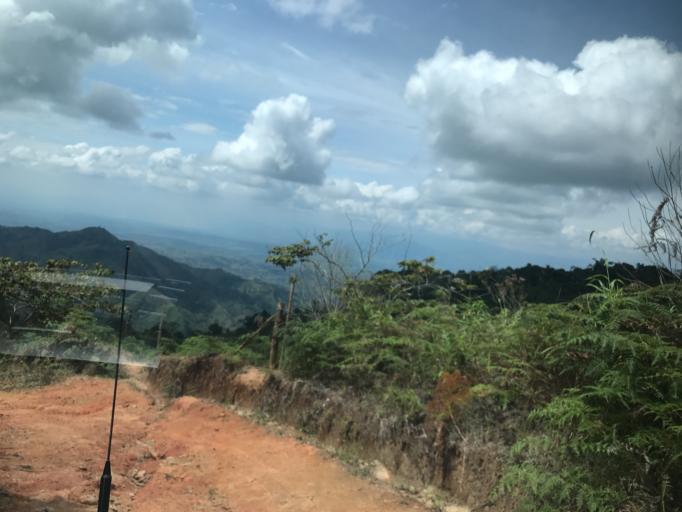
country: CO
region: Valle del Cauca
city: Obando
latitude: 4.5765
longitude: -75.8919
